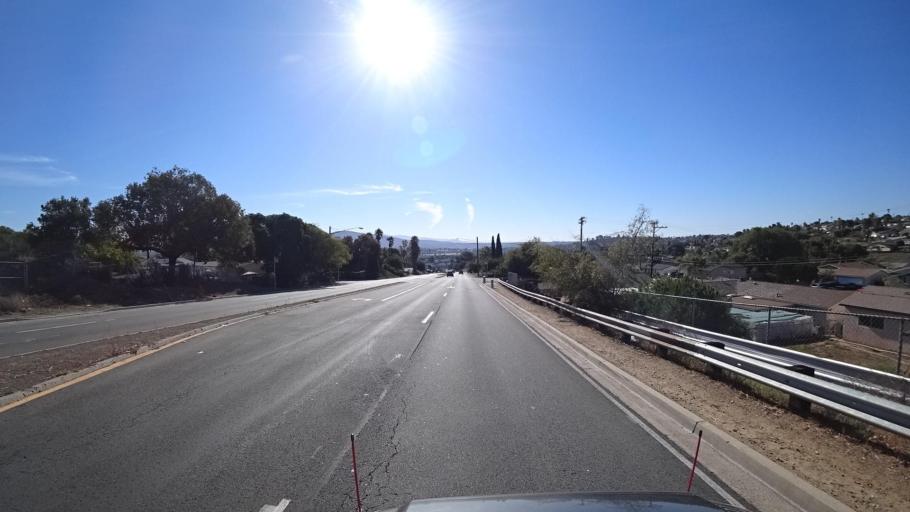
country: US
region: California
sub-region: San Diego County
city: La Presa
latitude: 32.7175
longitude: -117.0209
